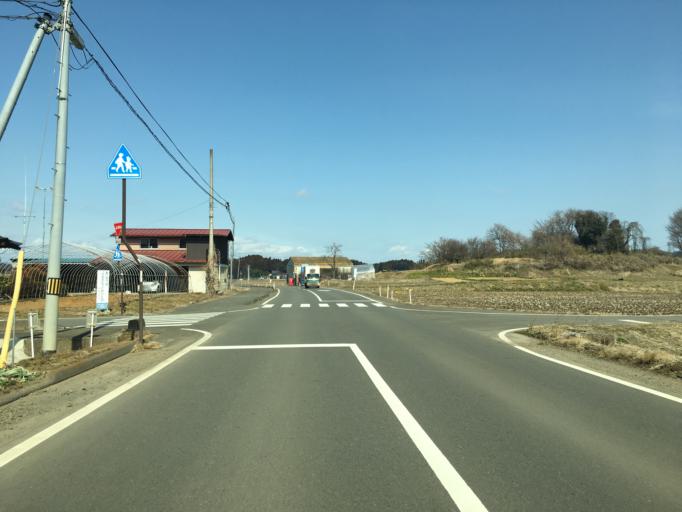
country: JP
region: Fukushima
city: Ishikawa
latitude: 37.1119
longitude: 140.2783
